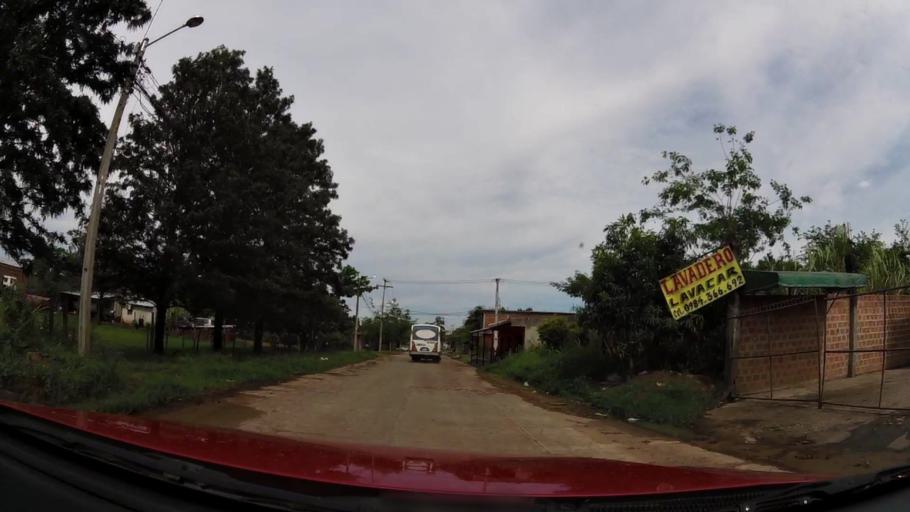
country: PY
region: Central
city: Limpio
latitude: -25.1742
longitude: -57.4726
